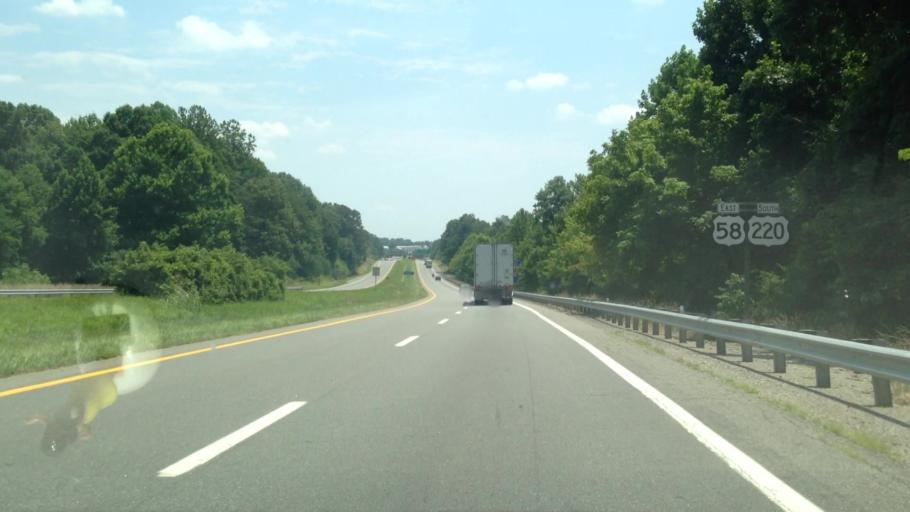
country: US
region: Virginia
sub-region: City of Martinsville
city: Martinsville
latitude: 36.6257
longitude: -79.8745
